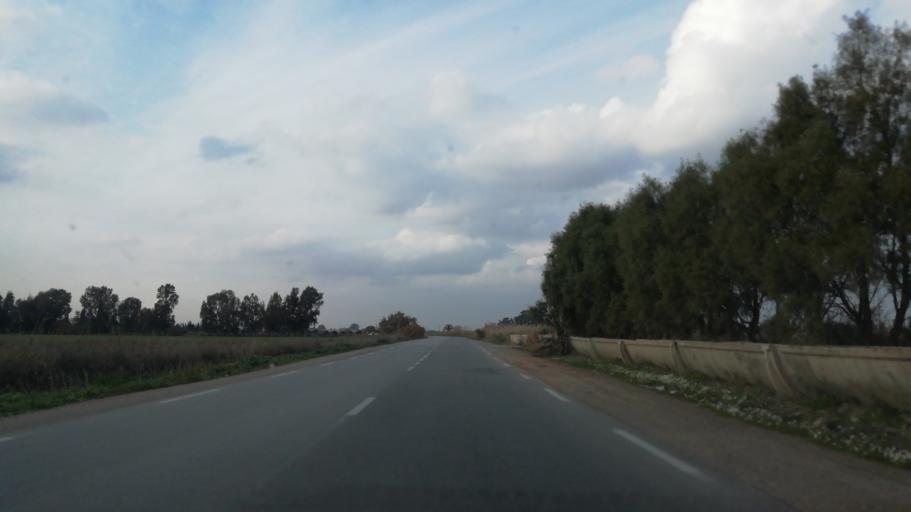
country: DZ
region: Mascara
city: Sig
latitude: 35.6480
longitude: 0.0250
